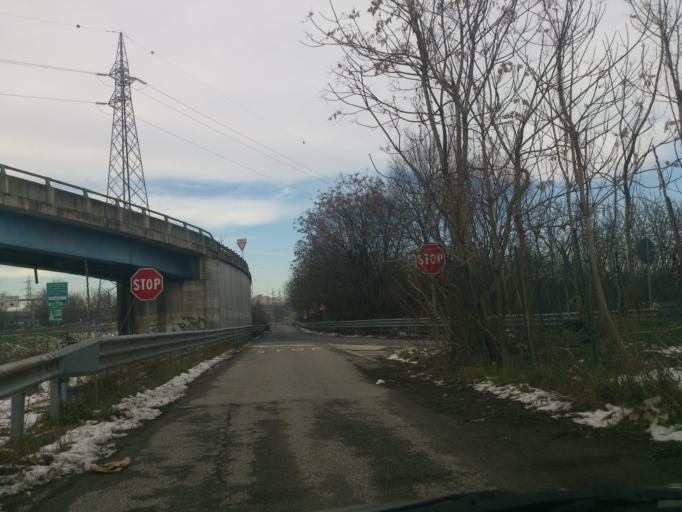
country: IT
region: Lombardy
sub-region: Citta metropolitana di Milano
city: Chiaravalle
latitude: 45.4247
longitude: 9.2493
